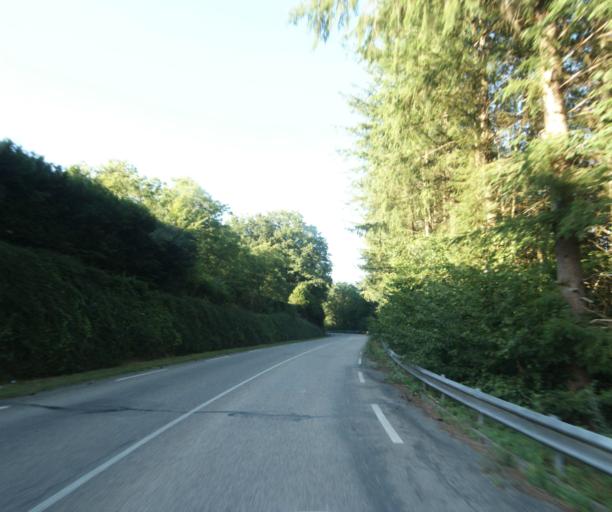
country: FR
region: Lorraine
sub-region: Departement des Vosges
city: Chantraine
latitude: 48.1426
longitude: 6.4533
